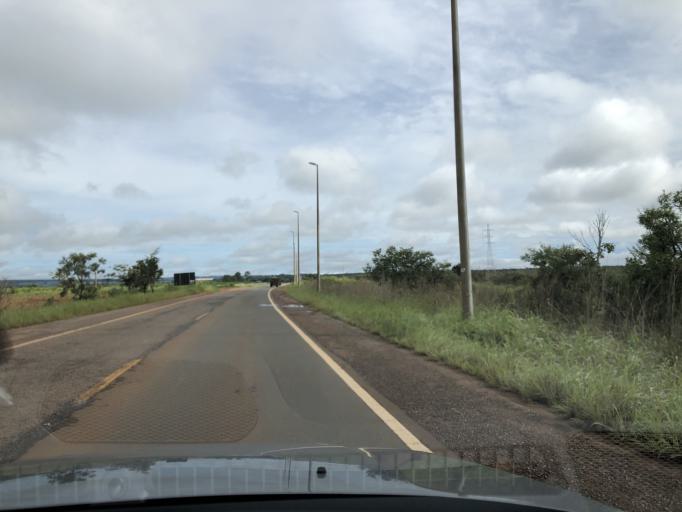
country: BR
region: Federal District
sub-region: Brasilia
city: Brasilia
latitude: -15.7240
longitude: -48.0863
